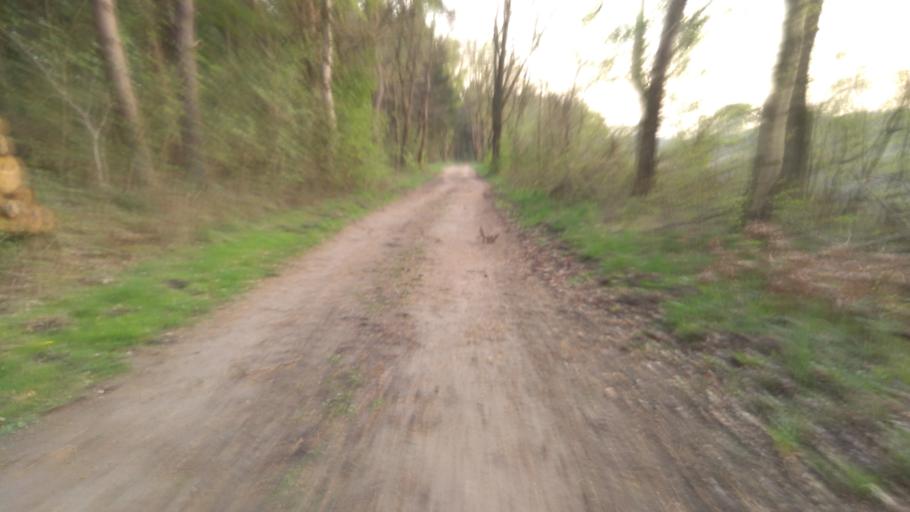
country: DE
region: Lower Saxony
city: Bliedersdorf
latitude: 53.4817
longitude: 9.5452
